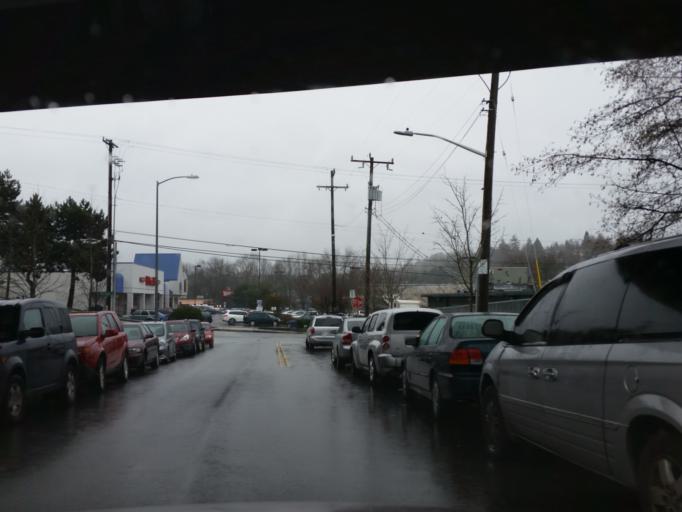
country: US
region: Washington
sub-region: King County
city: Seattle
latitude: 47.5778
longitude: -122.2993
